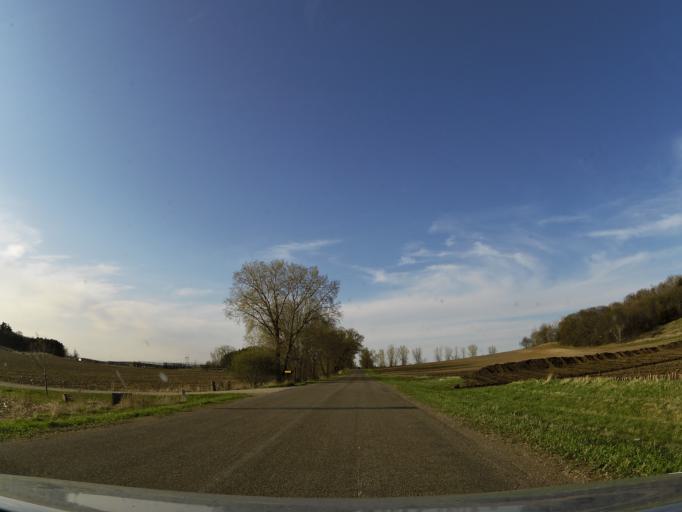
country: US
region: Minnesota
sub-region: Washington County
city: Afton
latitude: 44.8479
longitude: -92.7159
